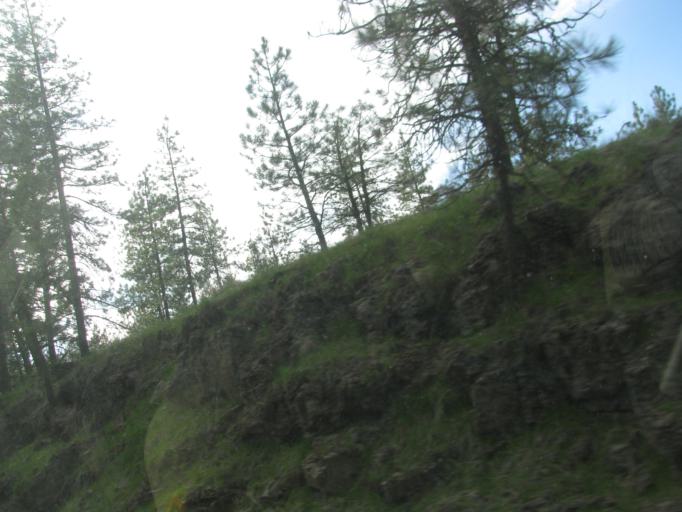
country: US
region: Washington
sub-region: Spokane County
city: Medical Lake
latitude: 47.3579
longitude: -117.8197
